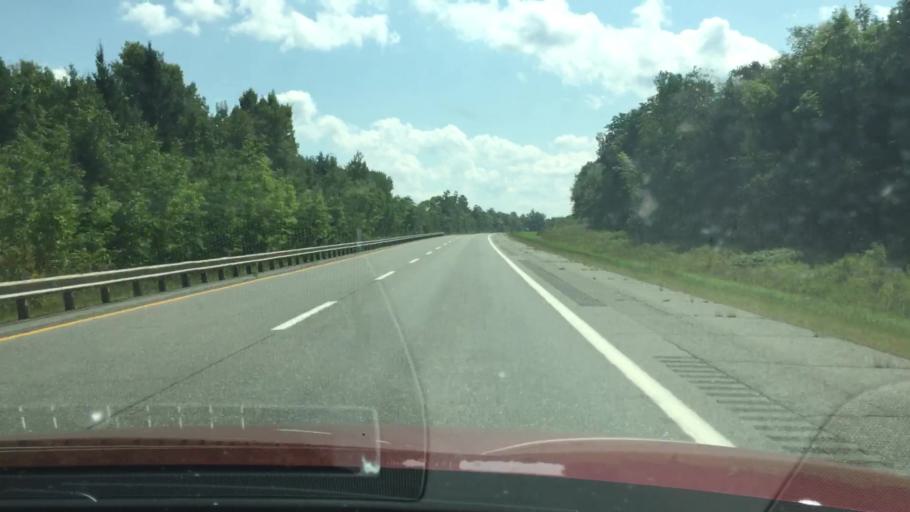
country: US
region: Maine
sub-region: Penobscot County
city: Lincoln
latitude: 45.4329
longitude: -68.5896
